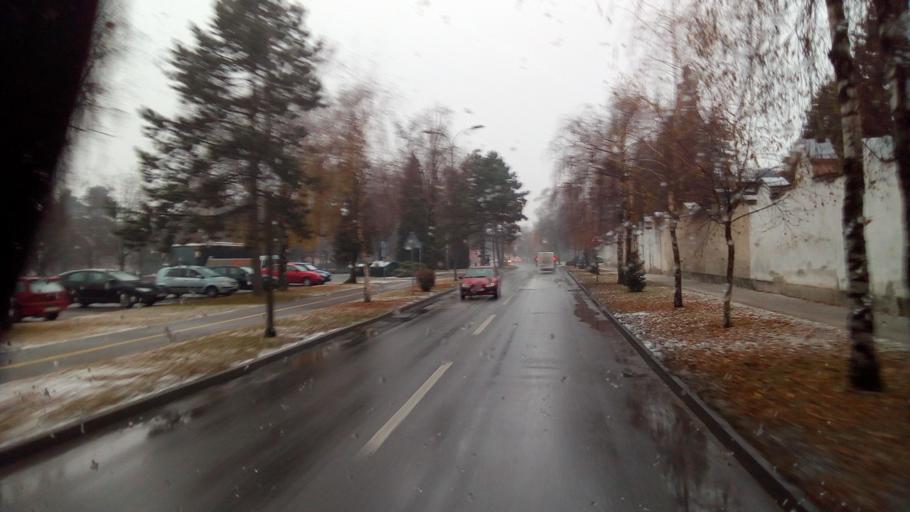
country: HR
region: Varazdinska
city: Varazdin
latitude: 46.3087
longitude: 16.3268
